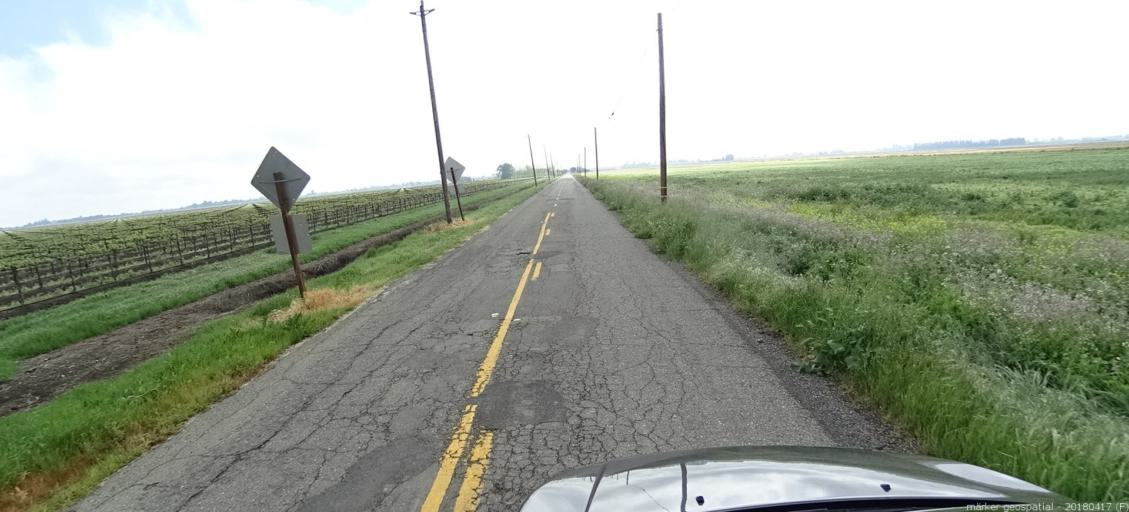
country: US
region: California
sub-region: Sacramento County
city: Walnut Grove
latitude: 38.2120
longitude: -121.5902
